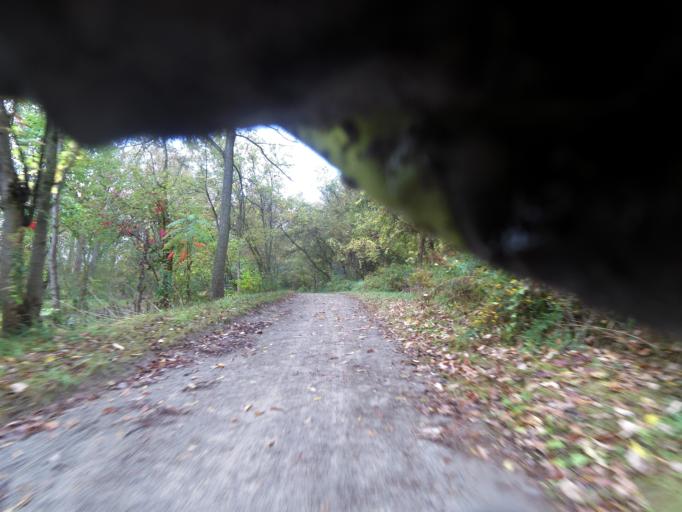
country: CA
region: Ontario
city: Brantford
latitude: 43.1427
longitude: -80.2163
